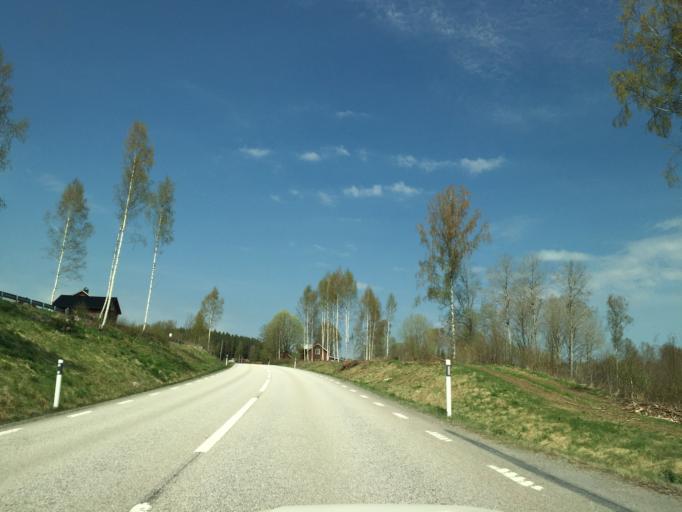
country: SE
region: Vaestra Goetaland
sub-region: Bengtsfors Kommun
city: Dals Langed
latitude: 58.8860
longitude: 12.2114
